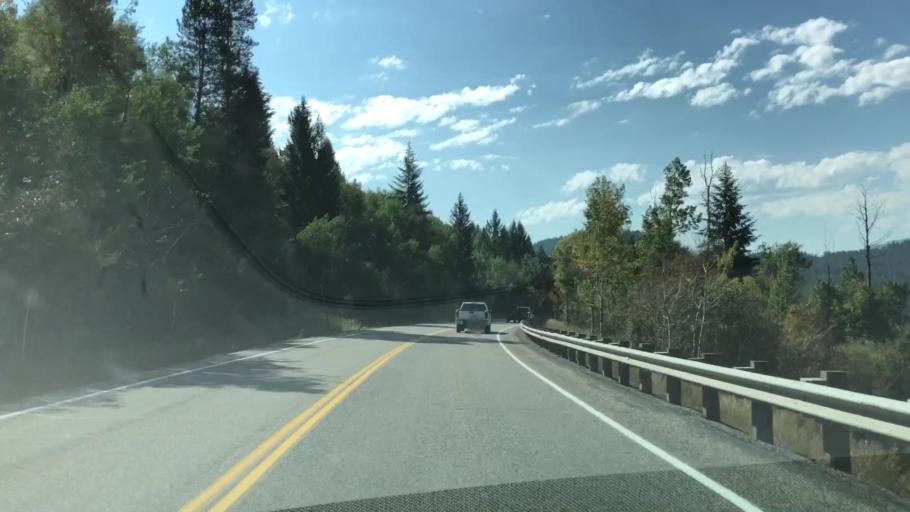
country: US
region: Idaho
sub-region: Teton County
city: Victor
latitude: 43.3226
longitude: -111.1663
